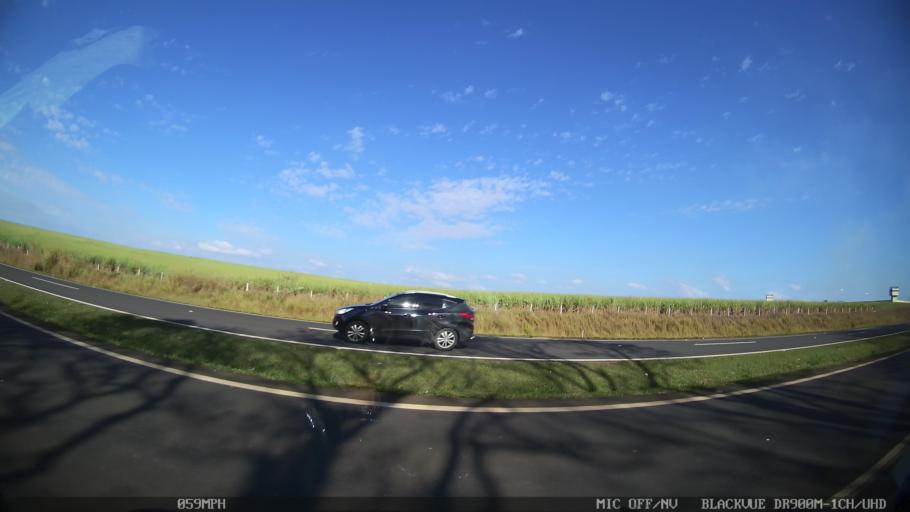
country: BR
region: Sao Paulo
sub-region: Piracicaba
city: Piracicaba
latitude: -22.6748
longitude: -47.5603
